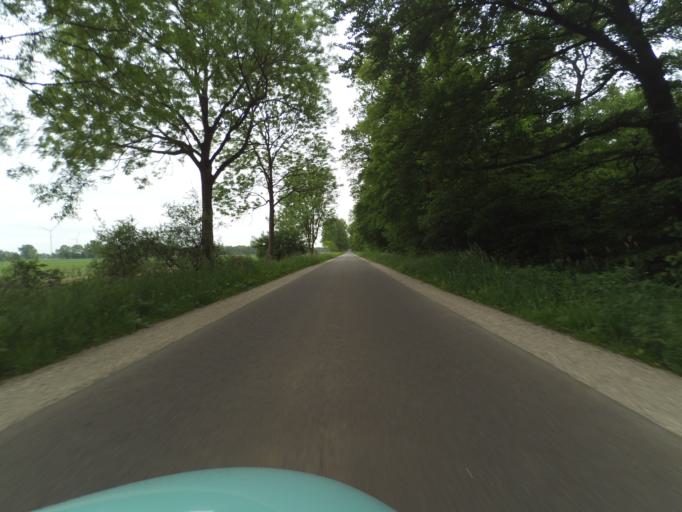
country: DE
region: Lower Saxony
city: Uetze
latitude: 52.4842
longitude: 10.1940
